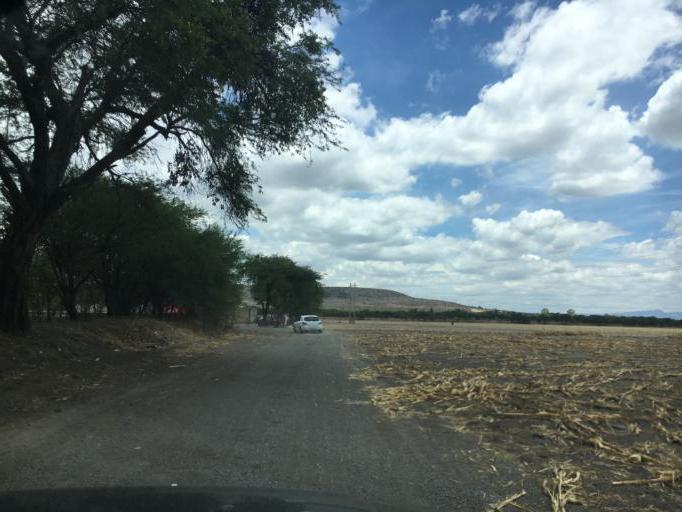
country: MX
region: Guanajuato
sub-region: Leon
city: Plan Guanajuato (La Sandia)
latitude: 20.9220
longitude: -101.7492
